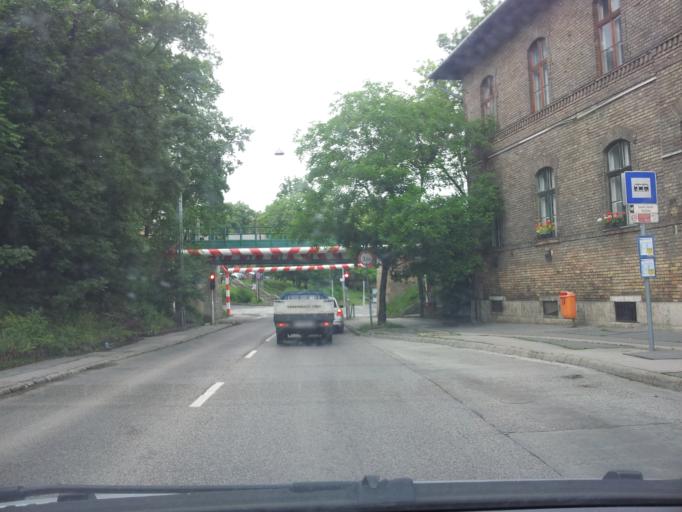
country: HU
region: Budapest
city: Budapest XII. keruelet
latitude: 47.5087
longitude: 19.0098
